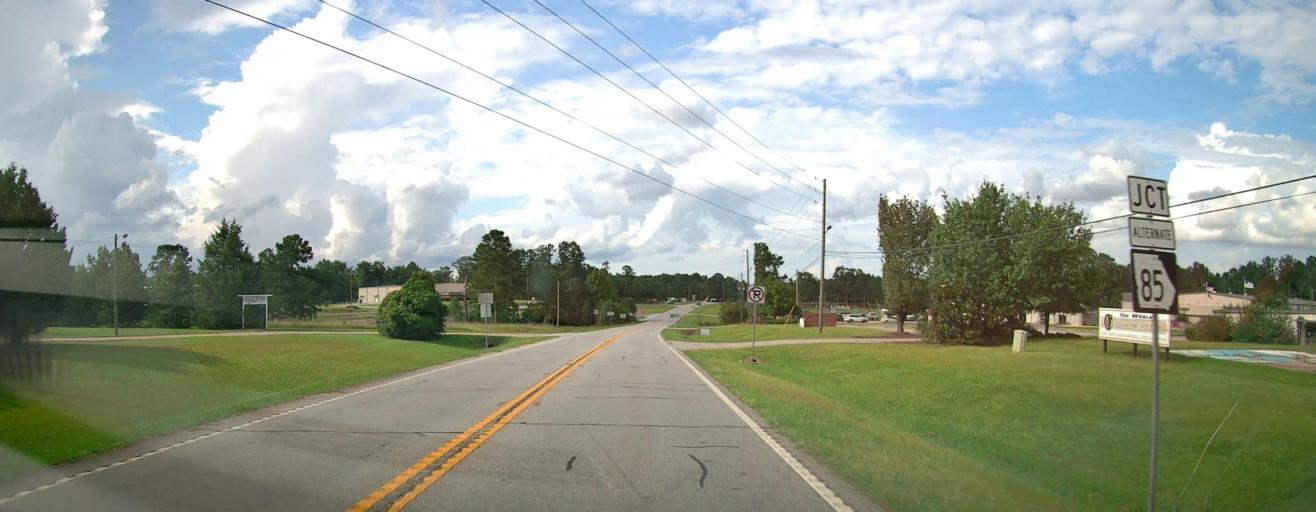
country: US
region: Georgia
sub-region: Meriwether County
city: Manchester
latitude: 32.9913
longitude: -84.5731
